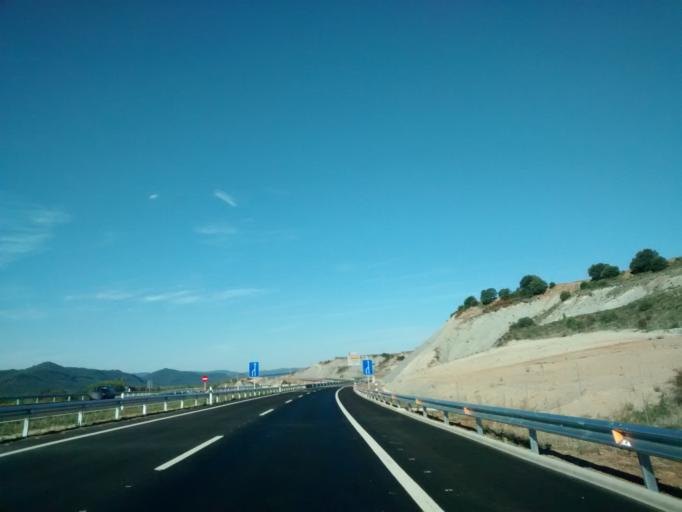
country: ES
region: Aragon
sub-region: Provincia de Huesca
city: Santa Cruz de la Seros
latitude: 42.5648
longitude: -0.7065
